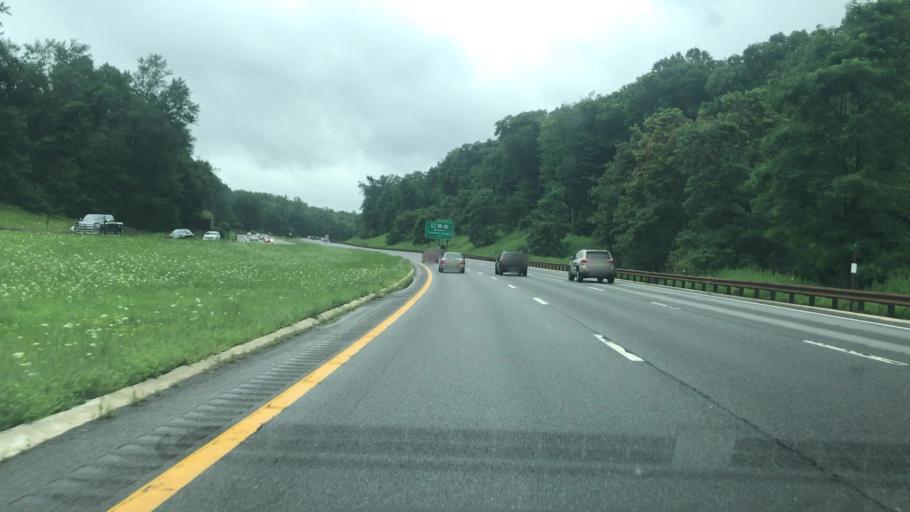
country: US
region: New York
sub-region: Westchester County
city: Shrub Oak
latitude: 41.3171
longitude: -73.8269
